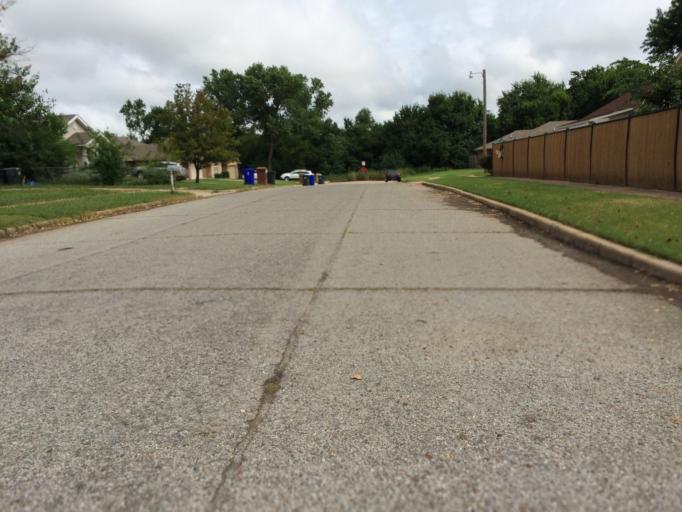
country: US
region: Oklahoma
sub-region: Cleveland County
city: Hall Park
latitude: 35.2247
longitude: -97.4183
